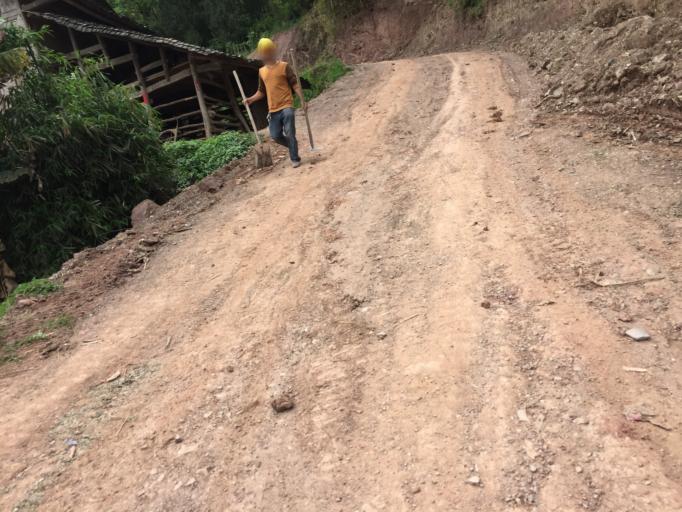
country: CN
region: Guizhou Sheng
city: Xujiaba
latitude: 27.6842
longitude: 108.0853
